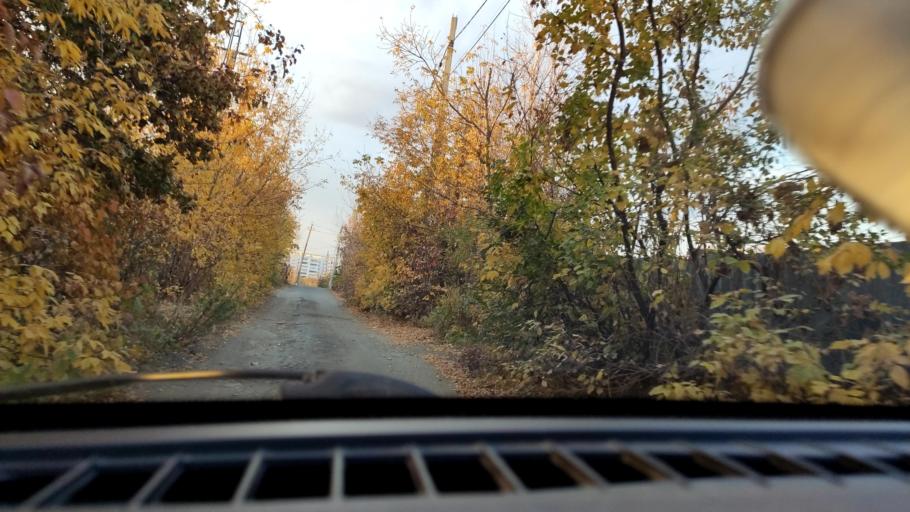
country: RU
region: Samara
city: Samara
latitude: 53.2724
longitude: 50.2286
